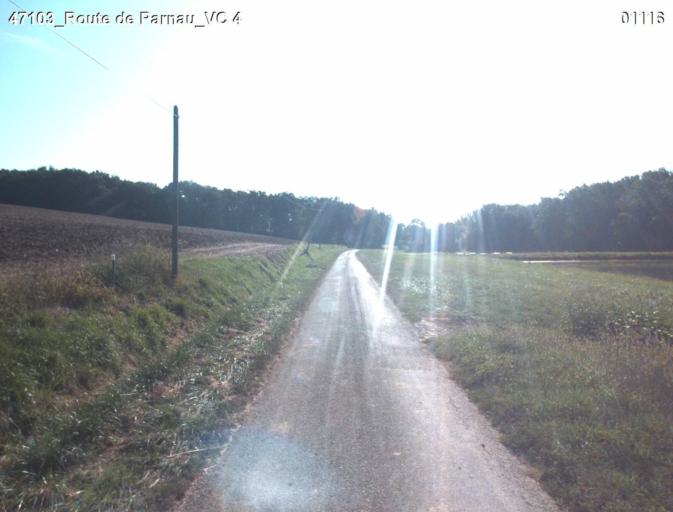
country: FR
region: Aquitaine
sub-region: Departement du Lot-et-Garonne
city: Nerac
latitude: 44.0811
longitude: 0.3420
